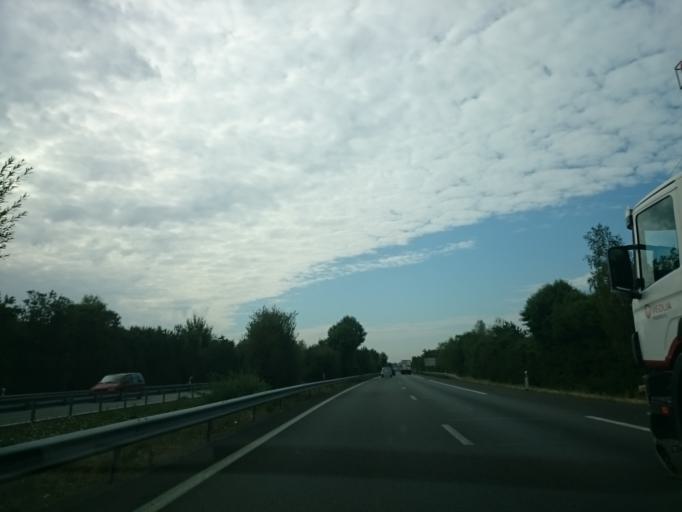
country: FR
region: Brittany
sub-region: Departement d'Ille-et-Vilaine
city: Crevin
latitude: 47.9514
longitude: -1.6792
